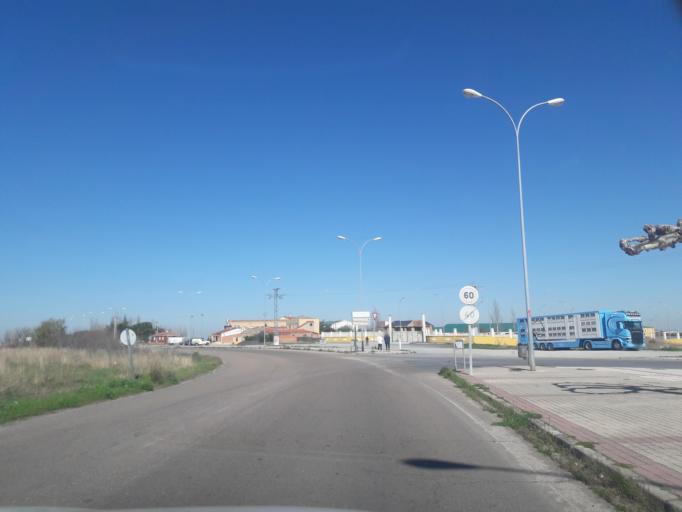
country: ES
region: Castille and Leon
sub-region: Provincia de Salamanca
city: Penaranda de Bracamonte
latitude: 40.9042
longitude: -5.2067
